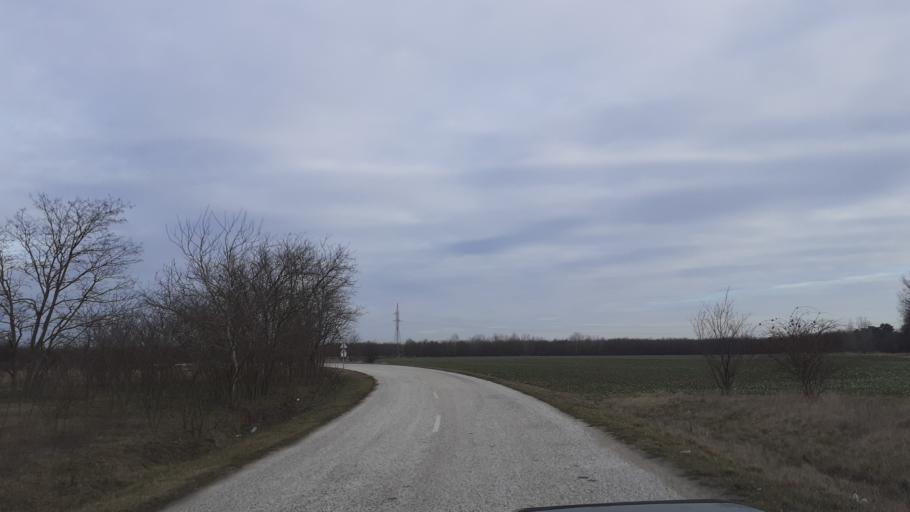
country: HU
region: Fejer
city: Szabadbattyan
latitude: 47.1195
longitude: 18.4024
